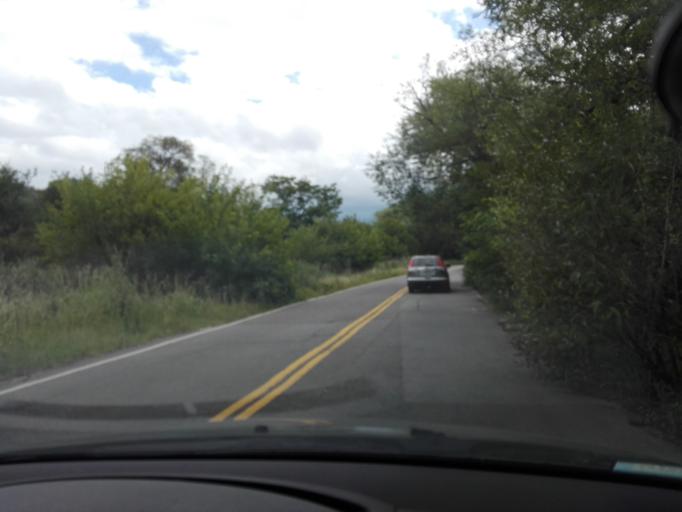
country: AR
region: Cordoba
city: Cuesta Blanca
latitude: -31.6050
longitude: -64.5535
